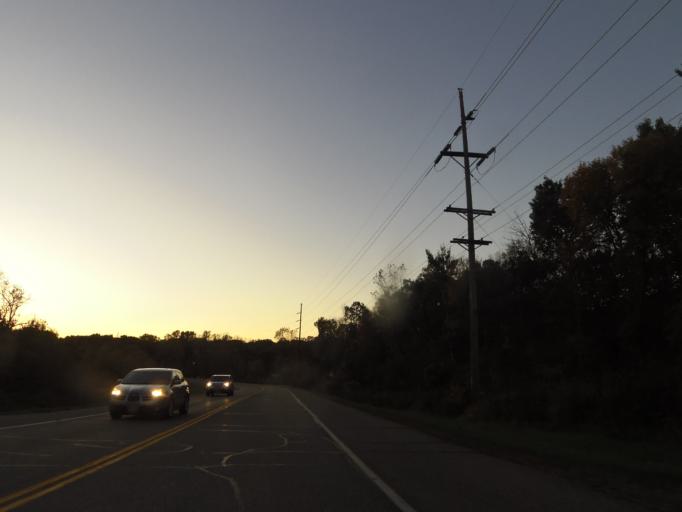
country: US
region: Minnesota
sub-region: Dakota County
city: Eagan
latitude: 44.7906
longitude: -93.1389
